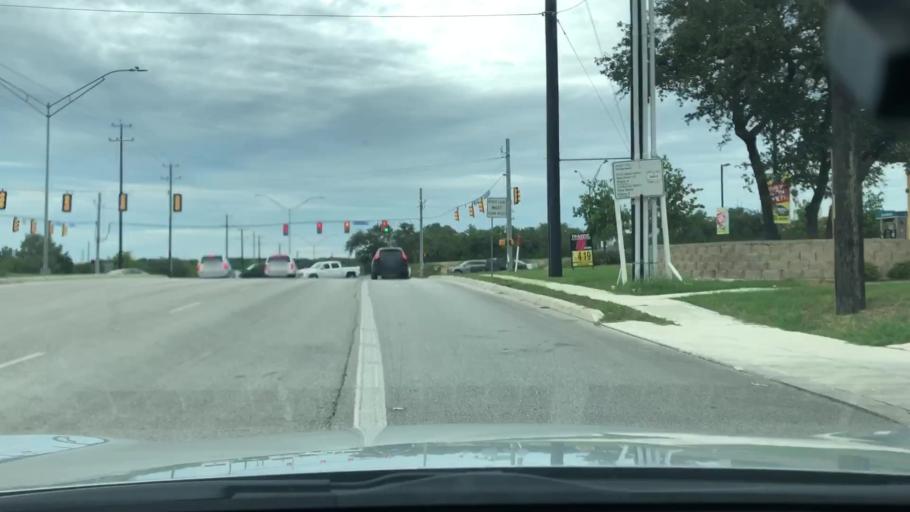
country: US
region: Texas
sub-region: Bexar County
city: Leon Valley
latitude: 29.4678
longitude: -98.6757
